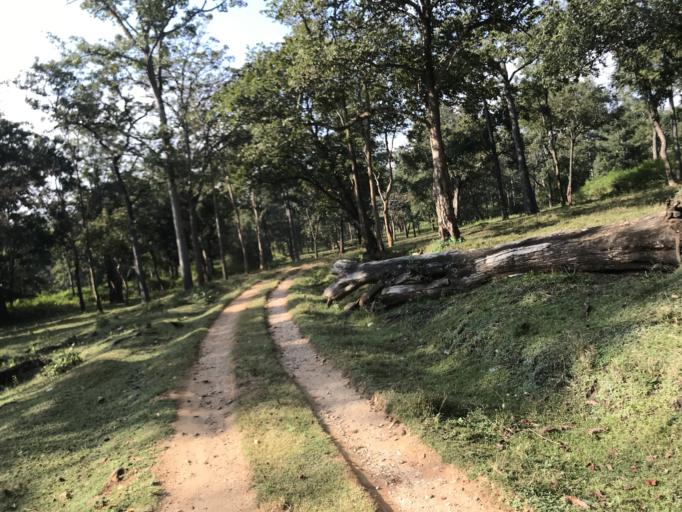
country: IN
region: Karnataka
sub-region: Mysore
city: Heggadadevankote
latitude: 11.9465
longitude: 76.2185
